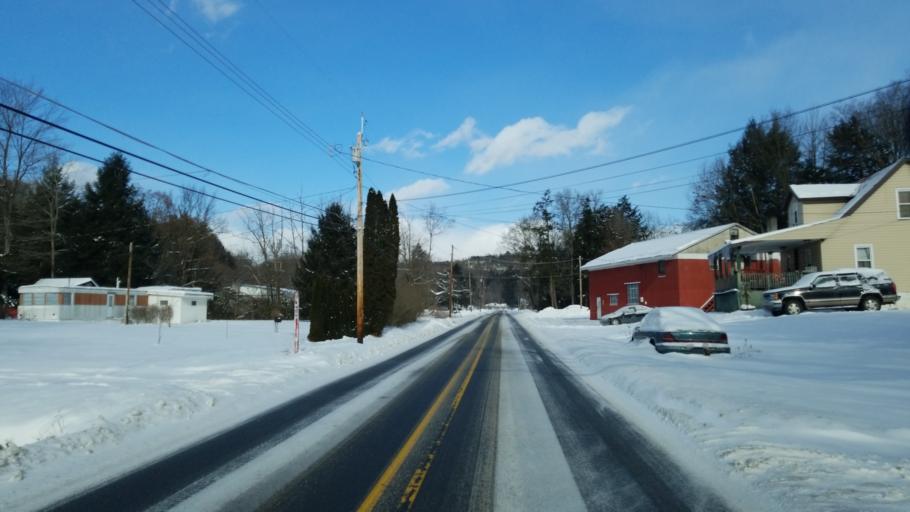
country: US
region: Pennsylvania
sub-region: Clearfield County
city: Hyde
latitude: 41.0080
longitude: -78.4689
